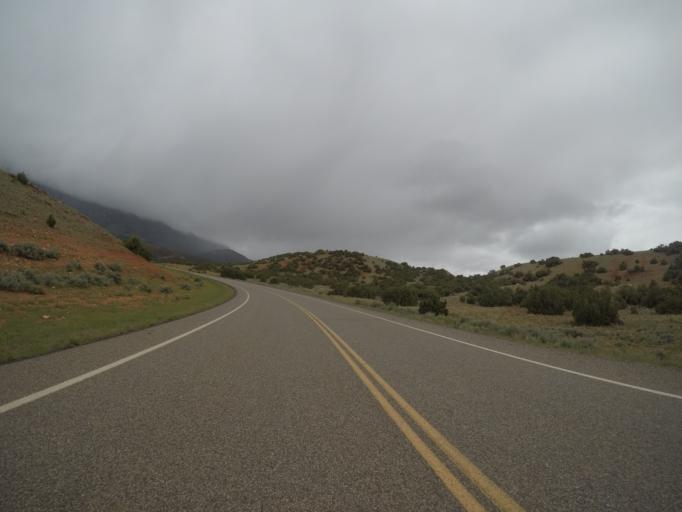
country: US
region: Wyoming
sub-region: Big Horn County
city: Lovell
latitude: 45.1040
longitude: -108.2376
